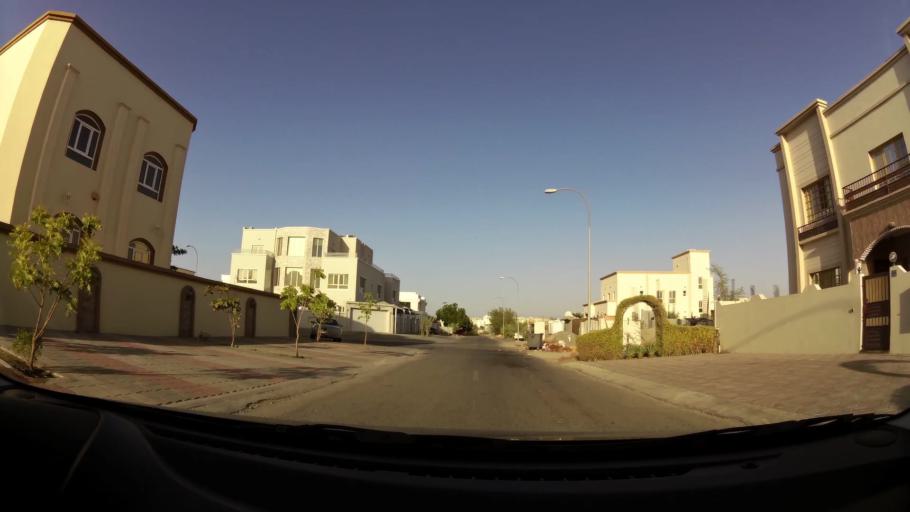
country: OM
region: Muhafazat Masqat
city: As Sib al Jadidah
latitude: 23.6103
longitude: 58.2230
